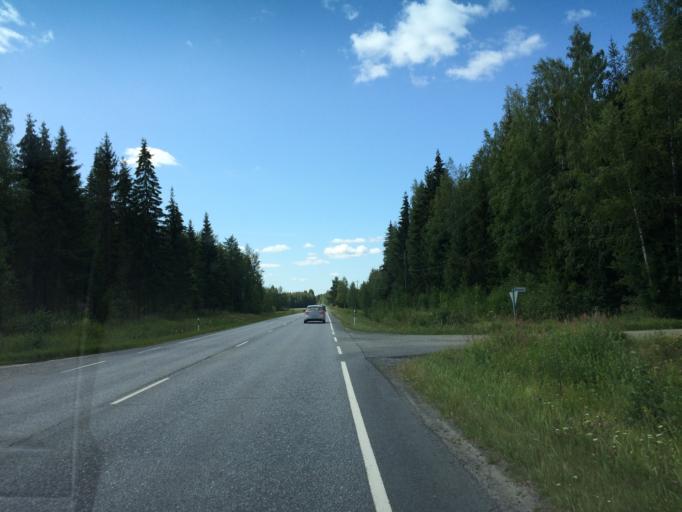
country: FI
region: Pirkanmaa
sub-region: Lounais-Pirkanmaa
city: Kiikoinen
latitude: 61.4863
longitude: 22.6665
